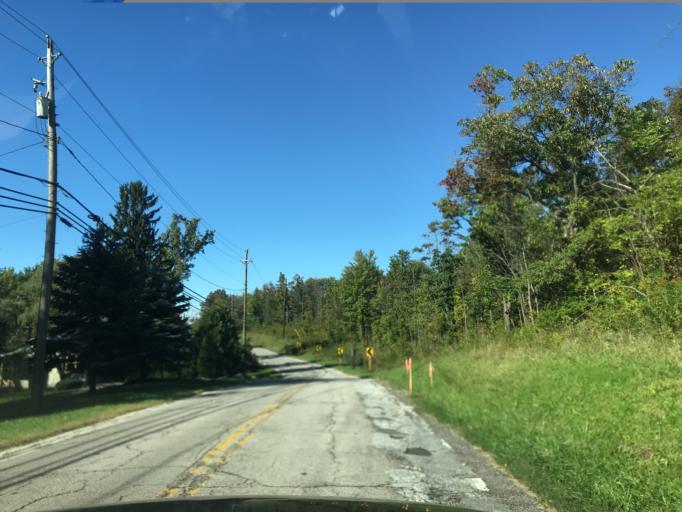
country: US
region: Ohio
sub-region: Lake County
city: Perry
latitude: 41.7133
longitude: -81.1766
